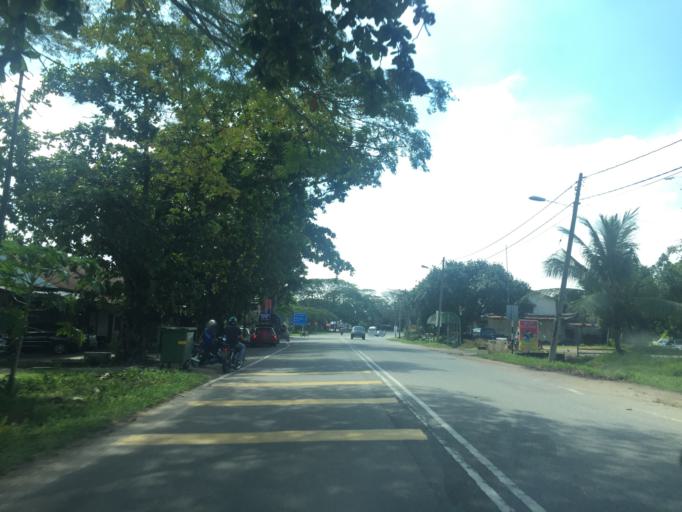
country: MY
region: Penang
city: Tasek Glugor
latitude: 5.4809
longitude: 100.5042
